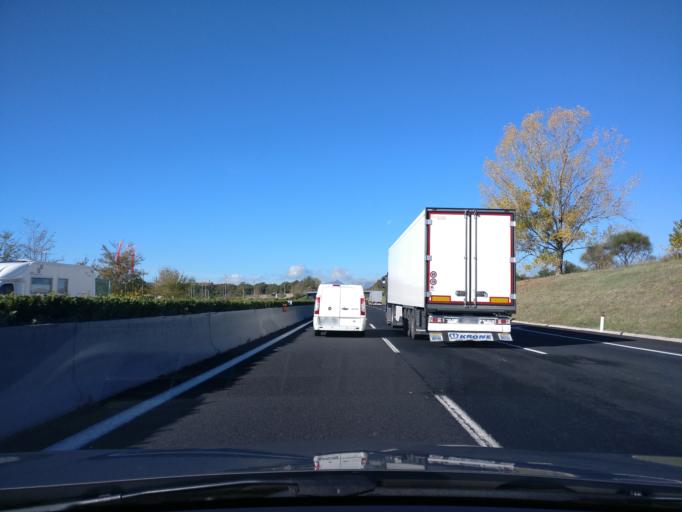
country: IT
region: Latium
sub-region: Provincia di Frosinone
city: Ceprano
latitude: 41.5460
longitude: 13.4809
